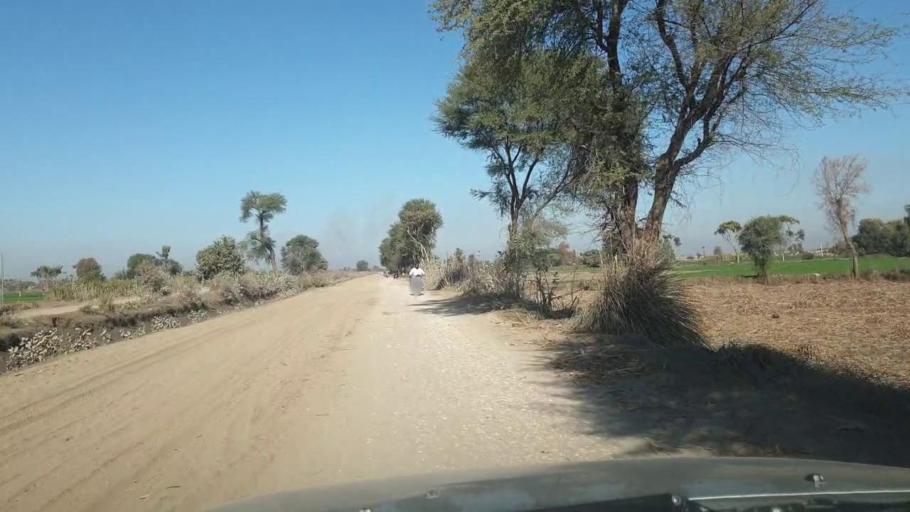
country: PK
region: Sindh
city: Ghotki
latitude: 28.0745
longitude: 69.3476
